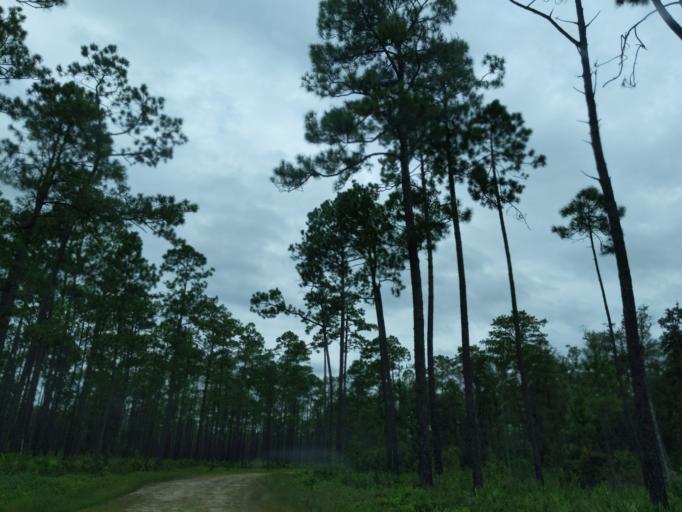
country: US
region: Florida
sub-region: Gadsden County
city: Midway
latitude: 30.3656
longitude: -84.4830
